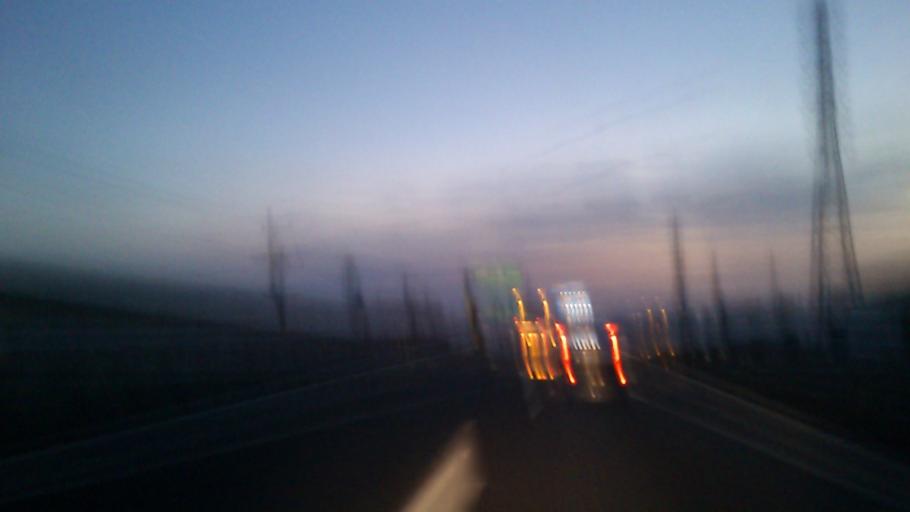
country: JP
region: Aichi
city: Komaki
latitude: 35.2972
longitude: 136.9302
